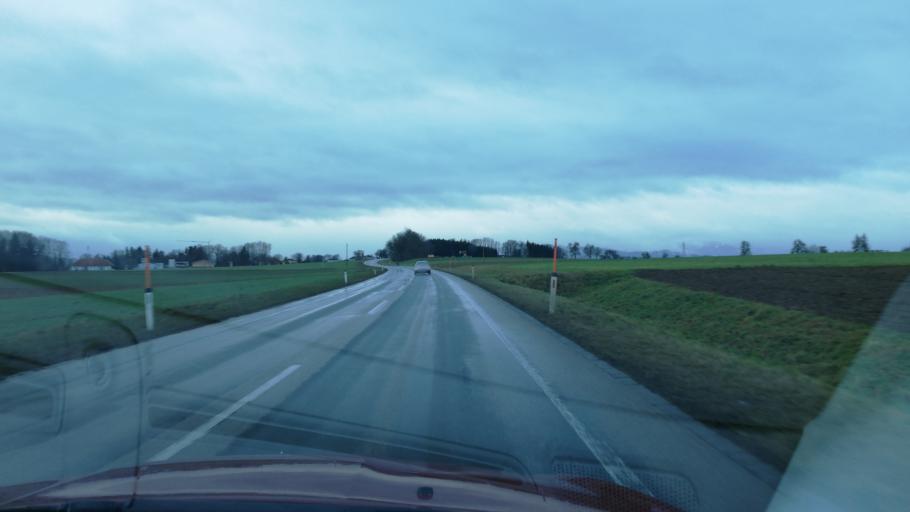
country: AT
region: Upper Austria
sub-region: Wels-Land
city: Sattledt
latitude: 48.0258
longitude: 14.0592
